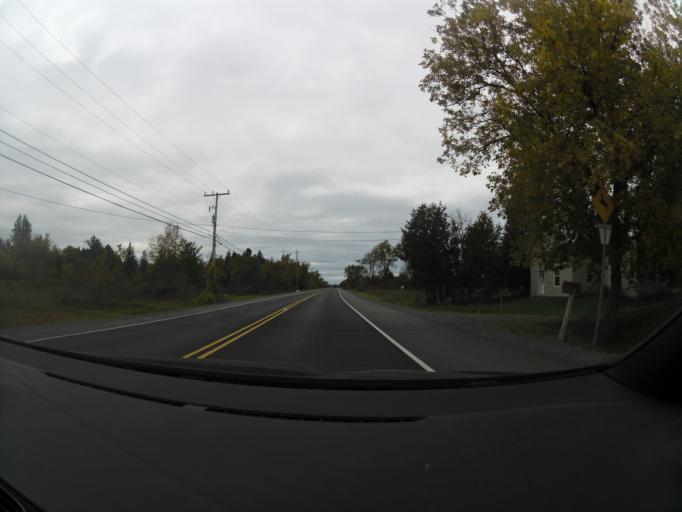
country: CA
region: Ontario
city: Bells Corners
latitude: 45.3951
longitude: -75.9870
